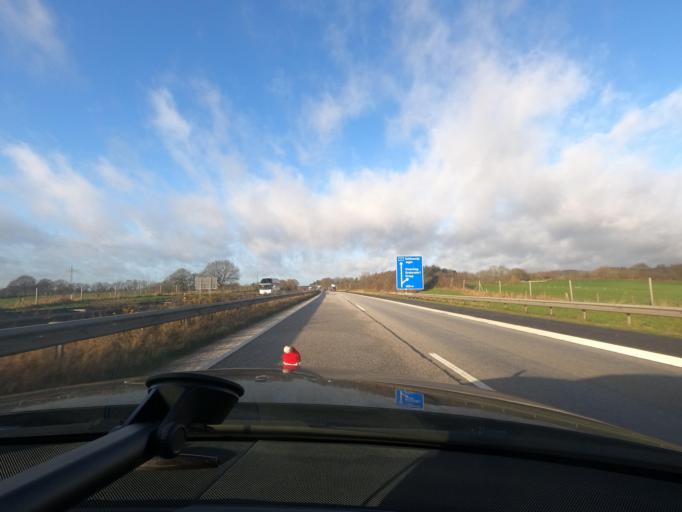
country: DE
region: Schleswig-Holstein
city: Brekendorf
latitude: 54.3961
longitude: 9.6465
